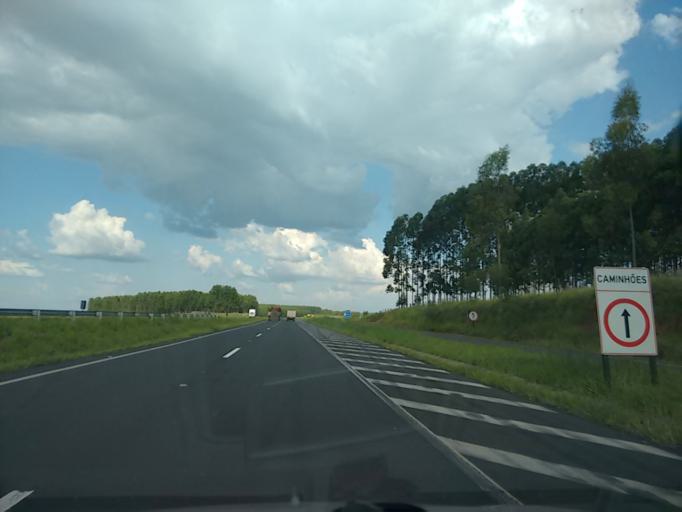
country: BR
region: Sao Paulo
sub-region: Duartina
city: Duartina
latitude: -22.3245
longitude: -49.4050
